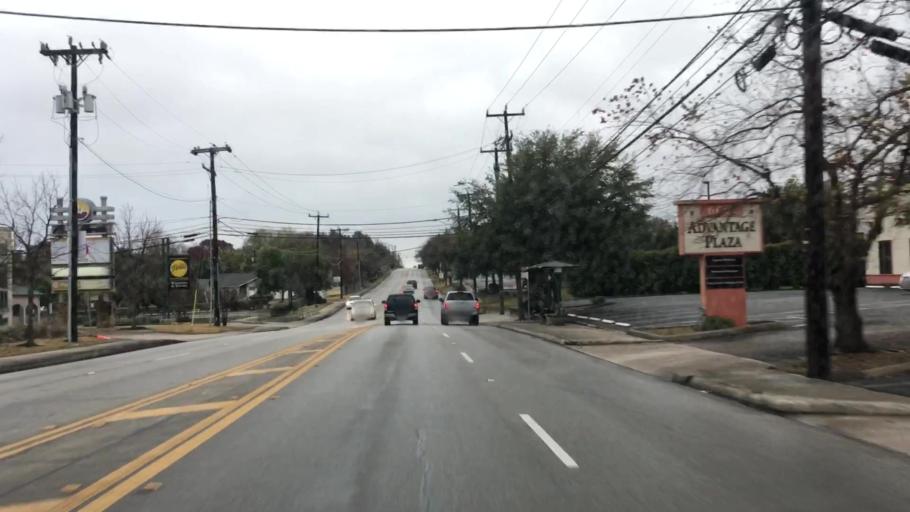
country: US
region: Texas
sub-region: Bexar County
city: Castle Hills
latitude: 29.5165
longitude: -98.5069
